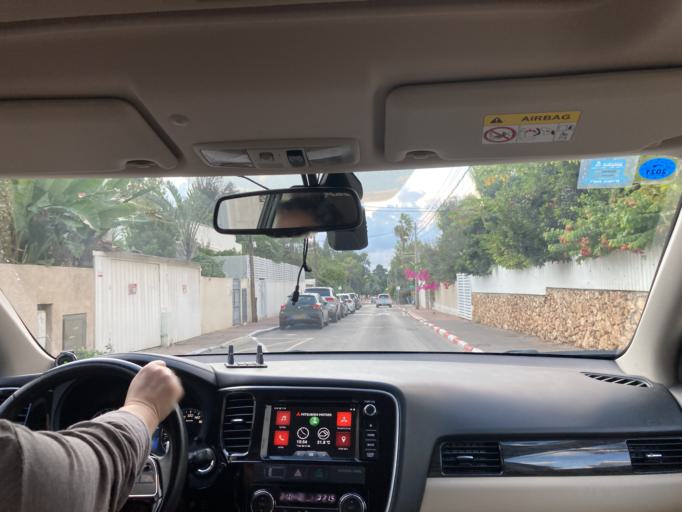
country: IL
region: Tel Aviv
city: Ramat HaSharon
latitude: 32.1511
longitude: 34.8391
